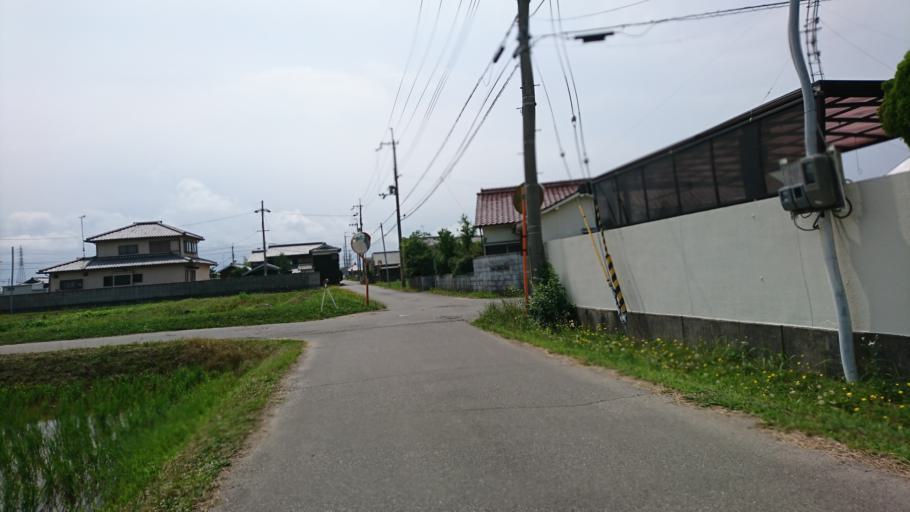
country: JP
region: Hyogo
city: Miki
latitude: 34.7491
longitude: 134.9337
